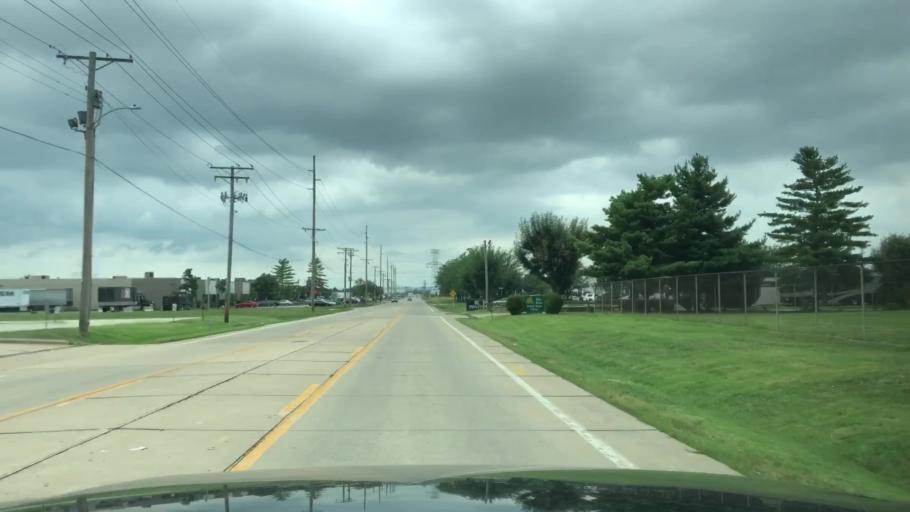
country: US
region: Missouri
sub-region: Saint Charles County
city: Saint Charles
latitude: 38.8212
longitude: -90.5009
